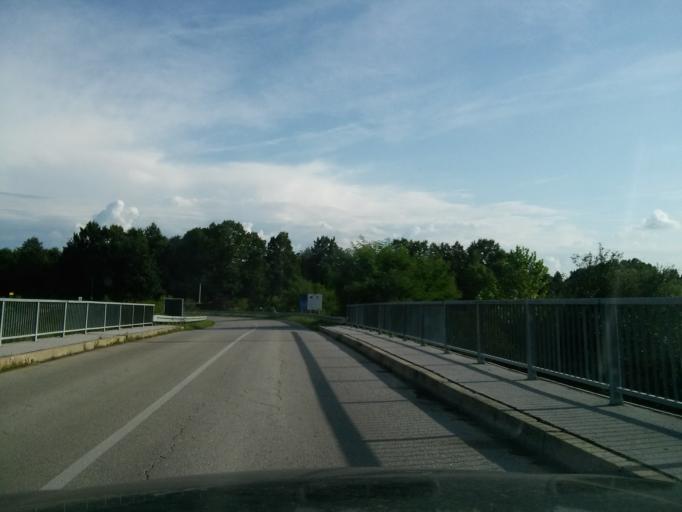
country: HR
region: Grad Zagreb
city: Horvati
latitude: 45.5478
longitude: 15.8574
